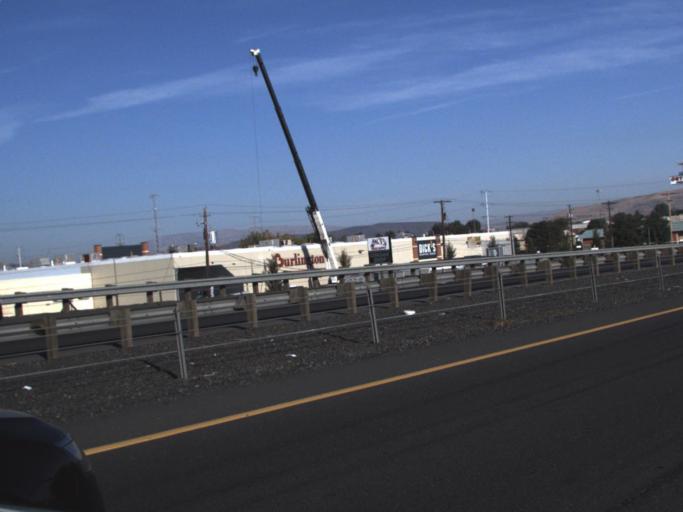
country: US
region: Washington
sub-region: Yakima County
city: Union Gap
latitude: 46.5648
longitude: -120.4722
